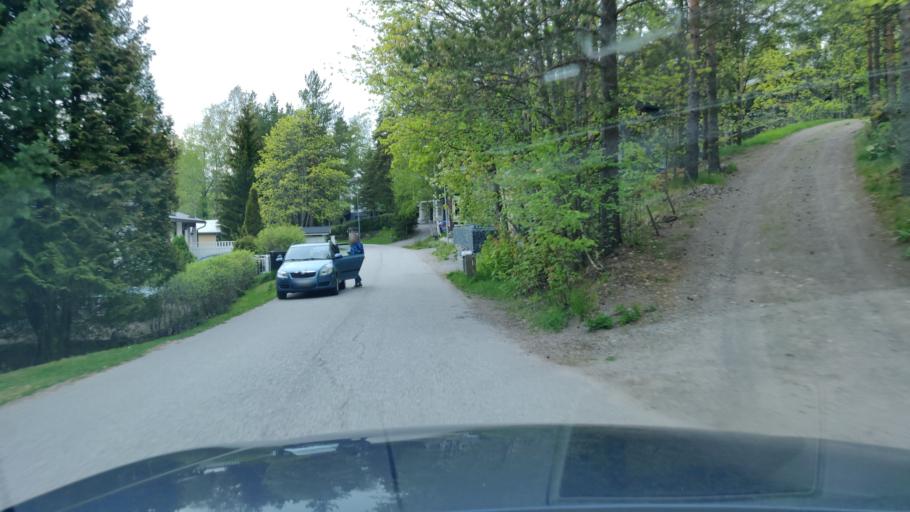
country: FI
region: Uusimaa
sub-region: Helsinki
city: Nurmijaervi
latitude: 60.3855
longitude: 24.7500
